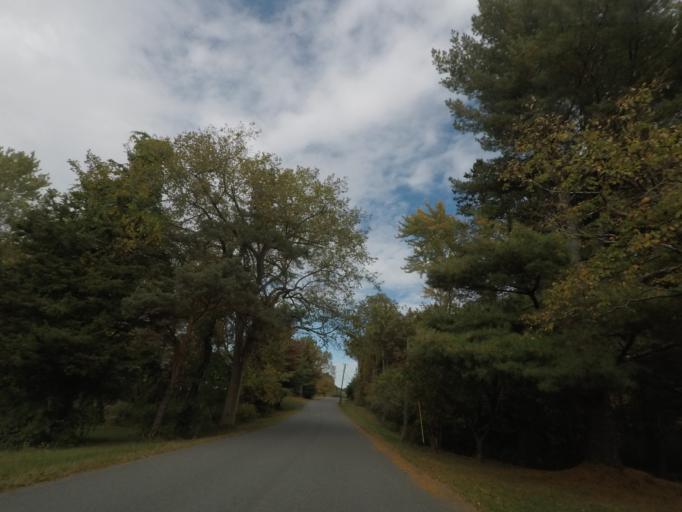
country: US
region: New York
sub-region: Rensselaer County
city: Nassau
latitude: 42.5297
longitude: -73.6454
